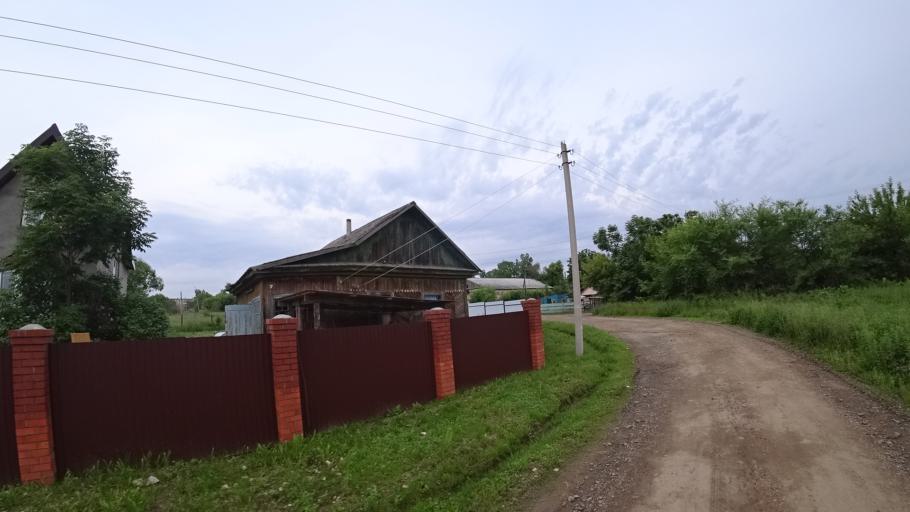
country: RU
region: Primorskiy
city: Novosysoyevka
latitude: 44.2264
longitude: 133.3541
